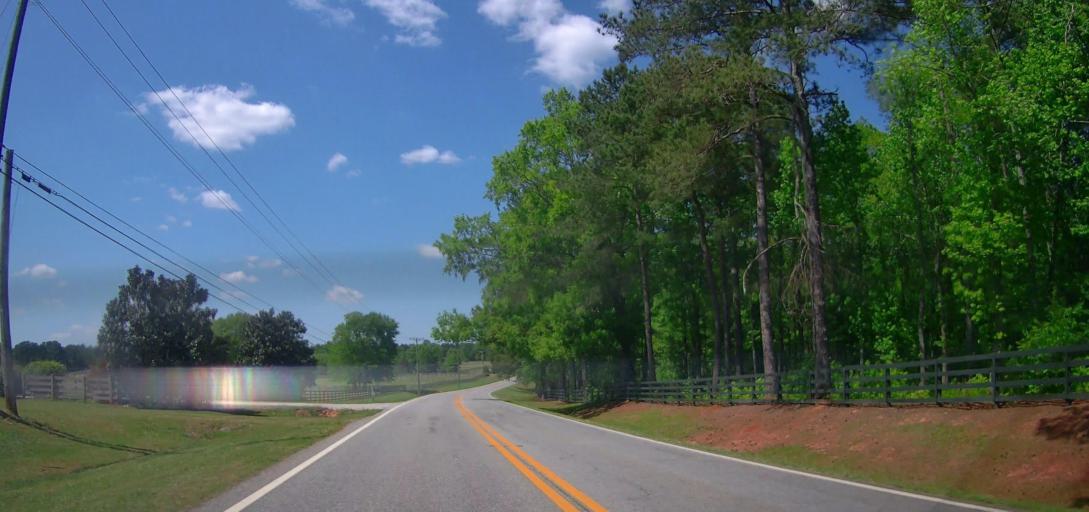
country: US
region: Georgia
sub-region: Putnam County
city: Eatonton
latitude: 33.2970
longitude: -83.3030
